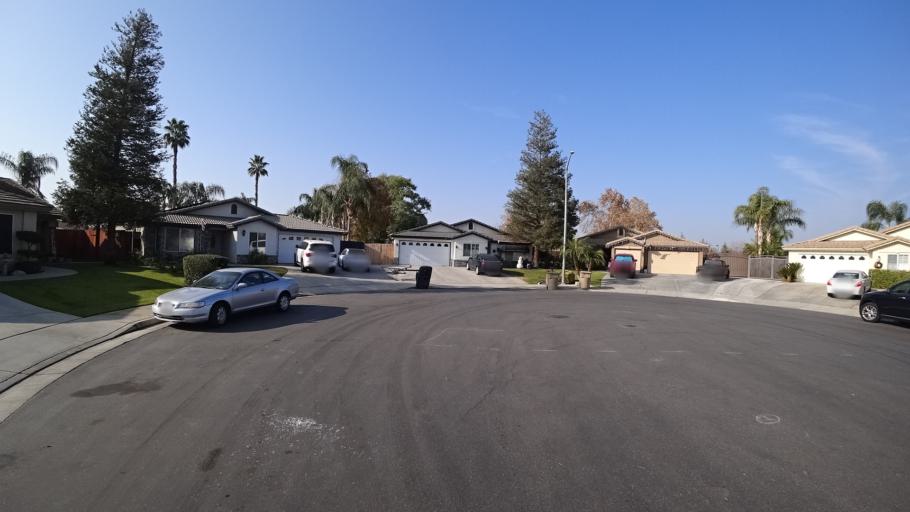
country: US
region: California
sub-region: Kern County
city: Greenacres
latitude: 35.4084
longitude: -119.1181
